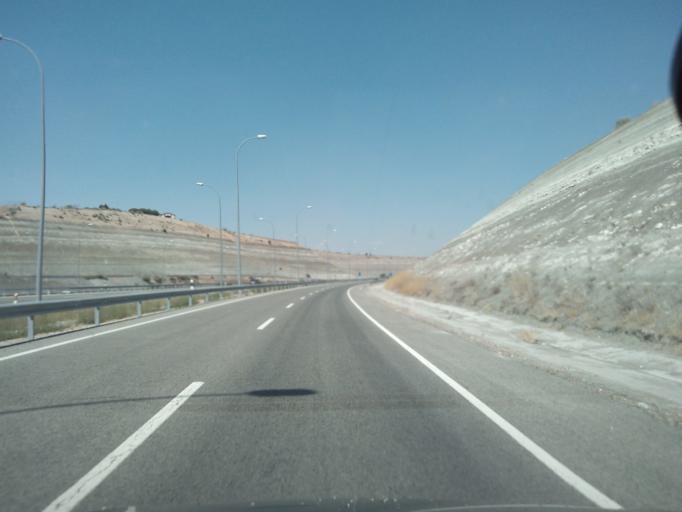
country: ES
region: Madrid
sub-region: Provincia de Madrid
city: San Fernando de Henares
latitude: 40.4608
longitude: -3.5188
